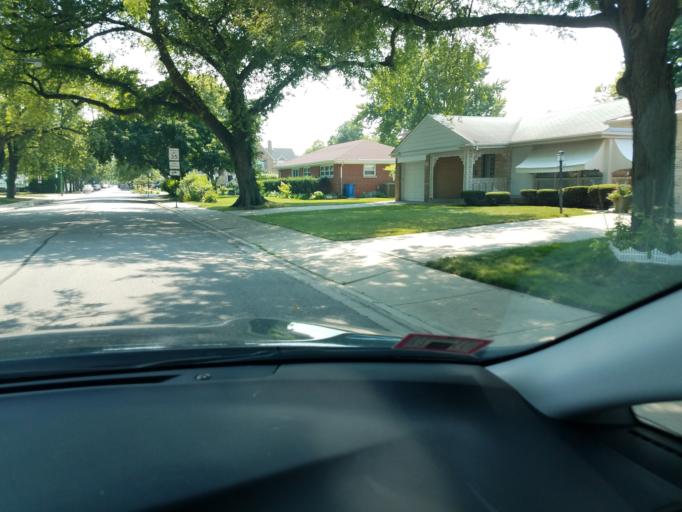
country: US
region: Illinois
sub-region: Cook County
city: Lincolnwood
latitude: 41.9933
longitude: -87.7472
